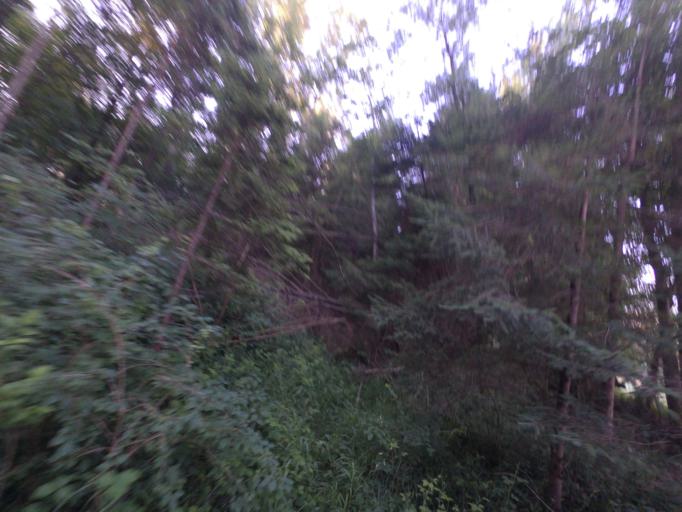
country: AT
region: Salzburg
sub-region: Politischer Bezirk Hallein
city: Puch bei Hallein
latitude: 47.7176
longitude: 13.0796
